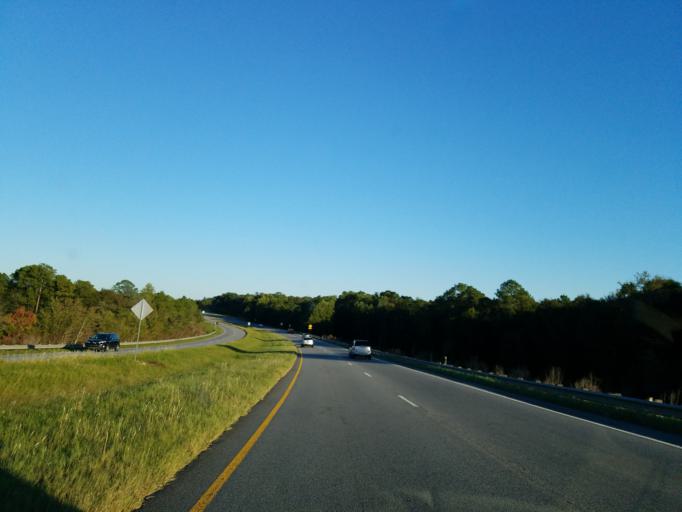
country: US
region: Georgia
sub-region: Worth County
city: Sylvester
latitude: 31.5117
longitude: -83.7756
